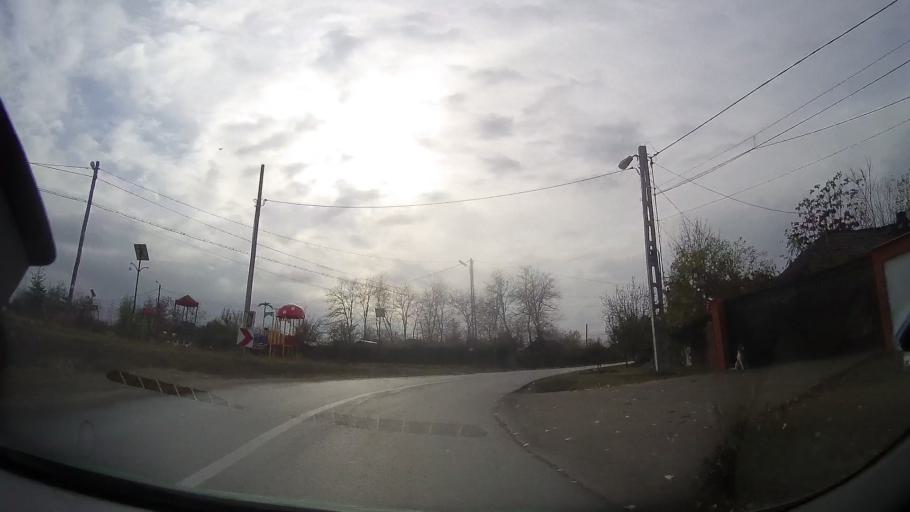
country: RO
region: Ialomita
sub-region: Comuna Maia
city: Maia
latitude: 44.7328
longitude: 26.4007
